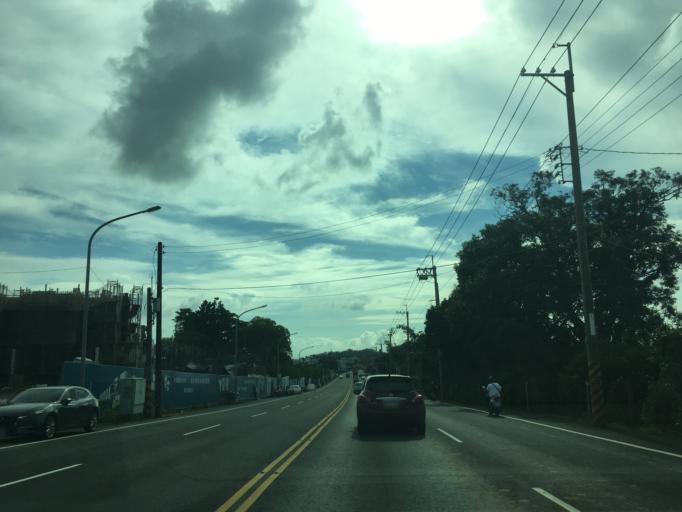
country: TW
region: Taiwan
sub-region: Chiayi
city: Jiayi Shi
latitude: 23.4421
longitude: 120.5203
